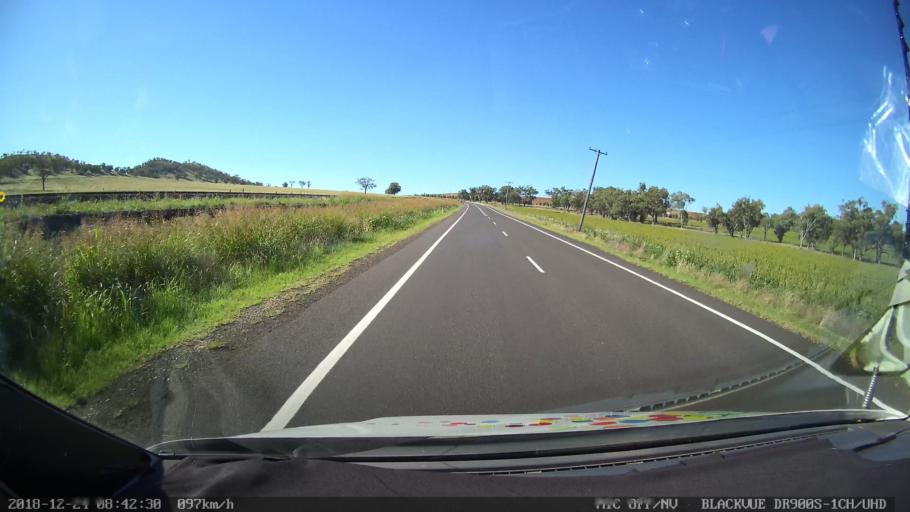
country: AU
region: New South Wales
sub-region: Liverpool Plains
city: Quirindi
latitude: -31.3756
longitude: 150.6429
